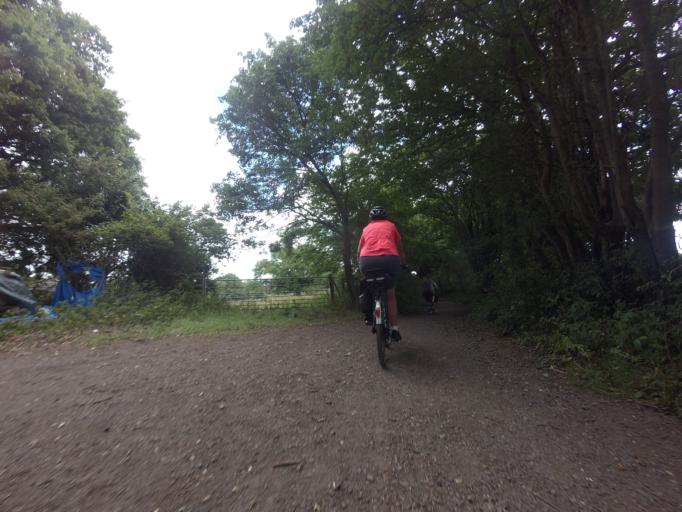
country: GB
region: England
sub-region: East Sussex
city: Hailsham
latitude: 50.8331
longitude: 0.2348
